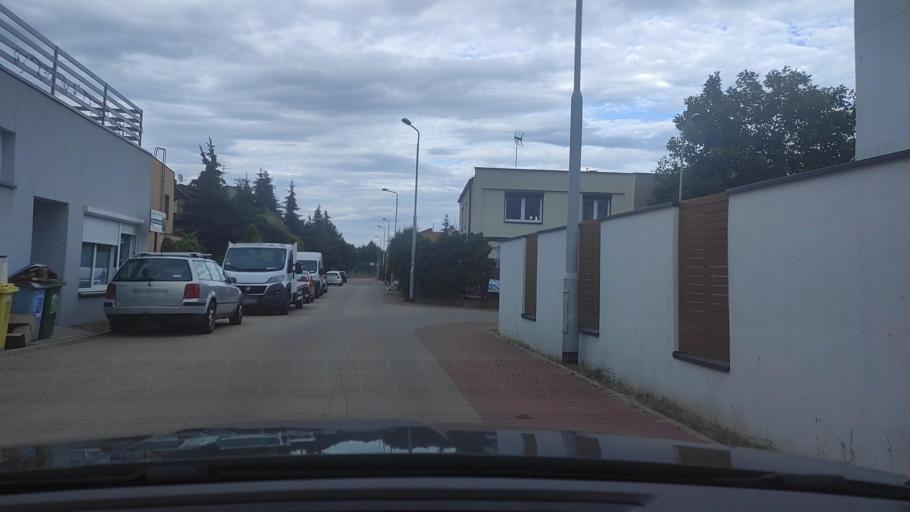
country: PL
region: Greater Poland Voivodeship
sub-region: Powiat poznanski
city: Swarzedz
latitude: 52.3967
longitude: 17.0589
